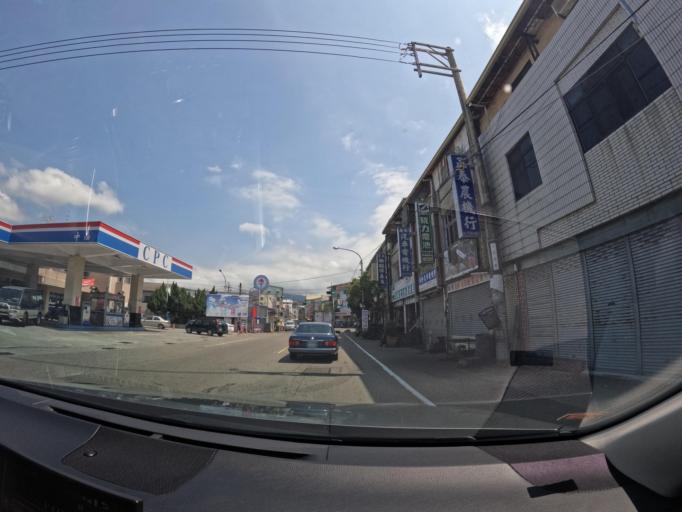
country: TW
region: Taiwan
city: Fengyuan
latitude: 24.3103
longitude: 120.8225
